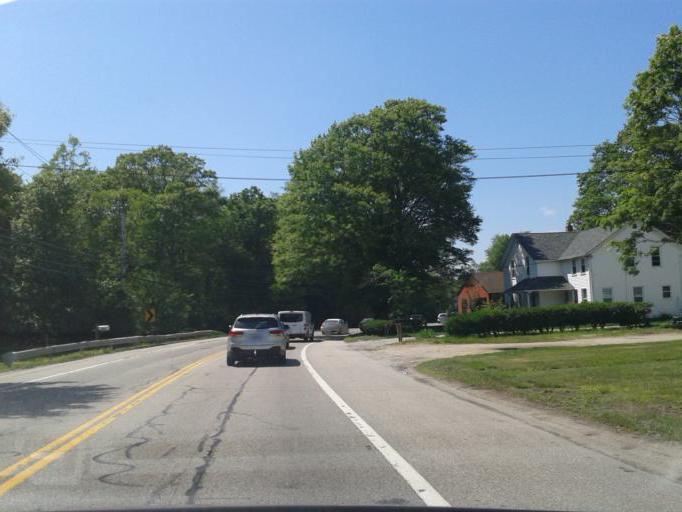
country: US
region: Rhode Island
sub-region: Washington County
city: Kingston
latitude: 41.4855
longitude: -71.5629
